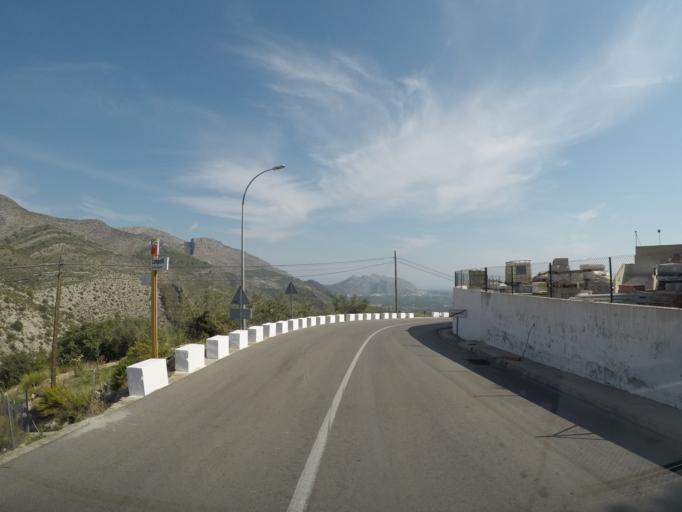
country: ES
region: Valencia
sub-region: Provincia de Alicante
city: Murla
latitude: 38.7811
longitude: -0.1014
